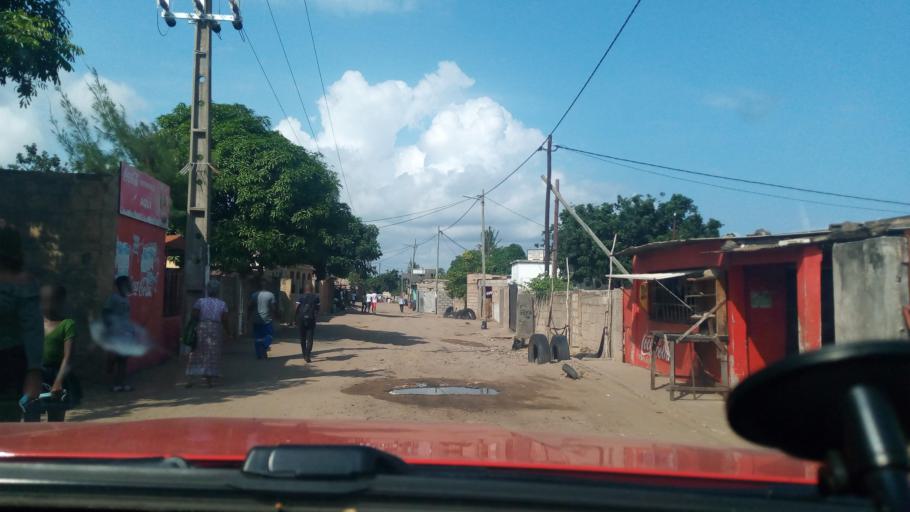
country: MZ
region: Maputo City
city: Maputo
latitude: -25.9190
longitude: 32.5623
